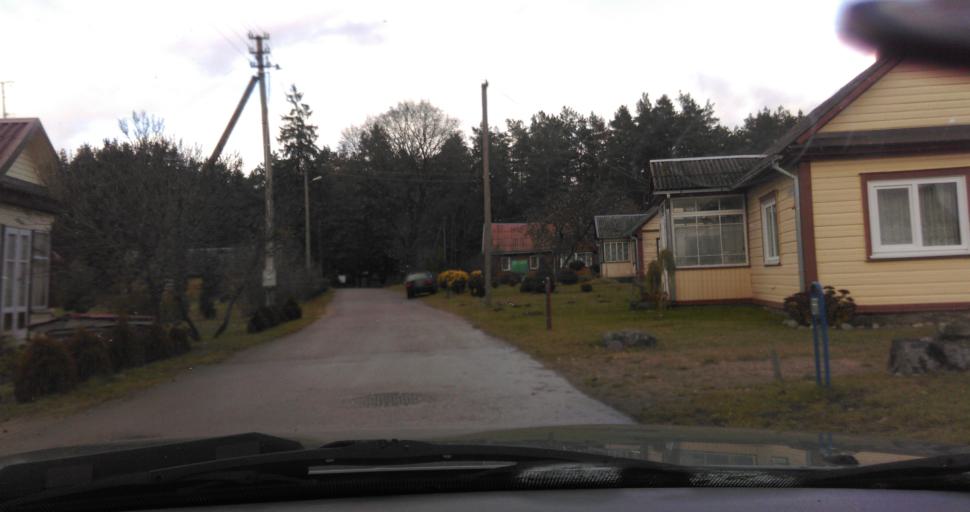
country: LT
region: Utenos apskritis
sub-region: Utena
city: Utena
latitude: 55.5893
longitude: 25.4980
